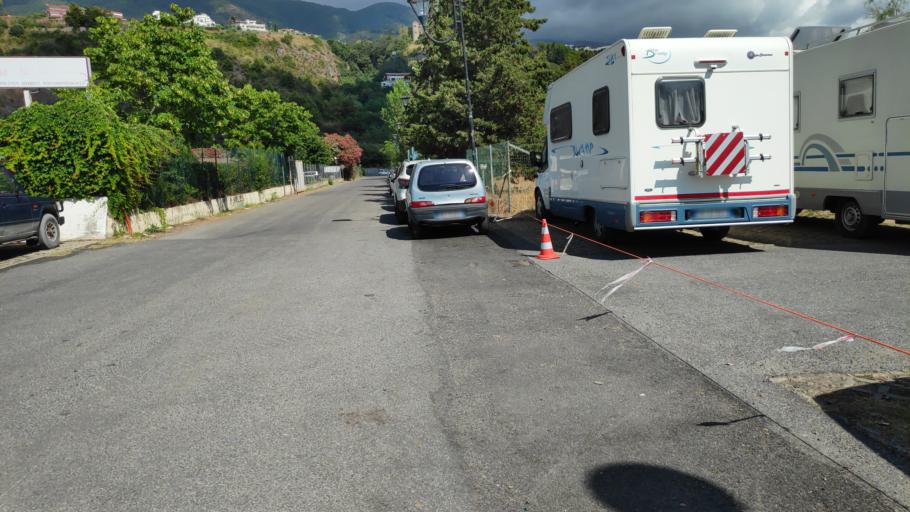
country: IT
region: Calabria
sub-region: Provincia di Cosenza
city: Praia a Mare
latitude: 39.8749
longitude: 15.7851
